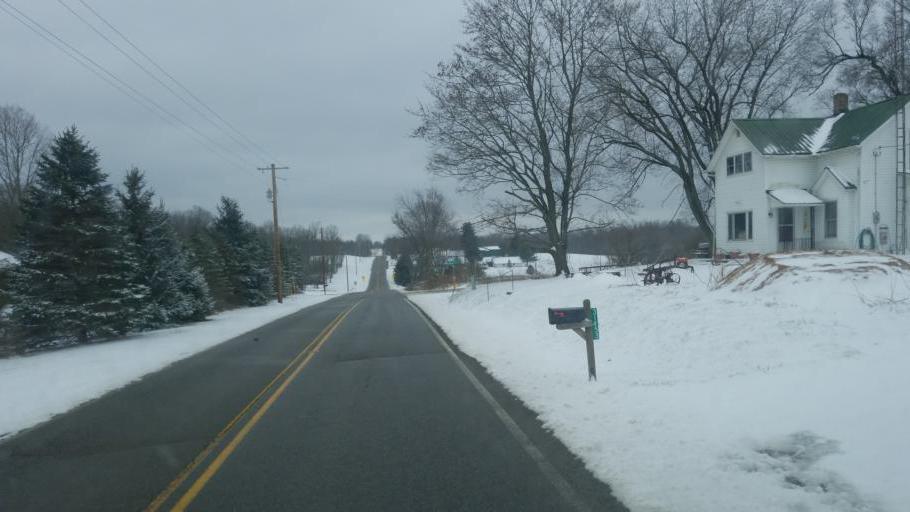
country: US
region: Ohio
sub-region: Knox County
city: Oak Hill
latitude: 40.4169
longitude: -82.1381
